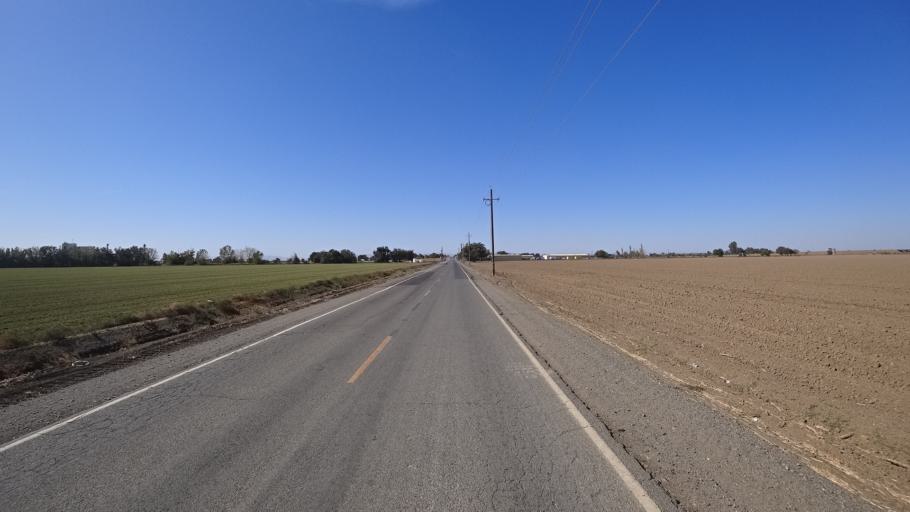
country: US
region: California
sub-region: Yolo County
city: Woodland
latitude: 38.6192
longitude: -121.7579
